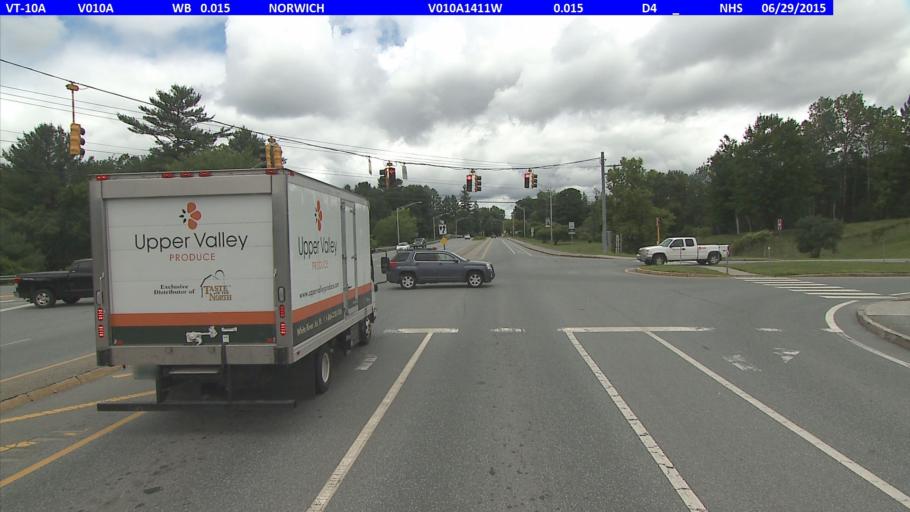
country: US
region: New Hampshire
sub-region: Grafton County
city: Hanover
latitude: 43.7078
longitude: -72.3070
